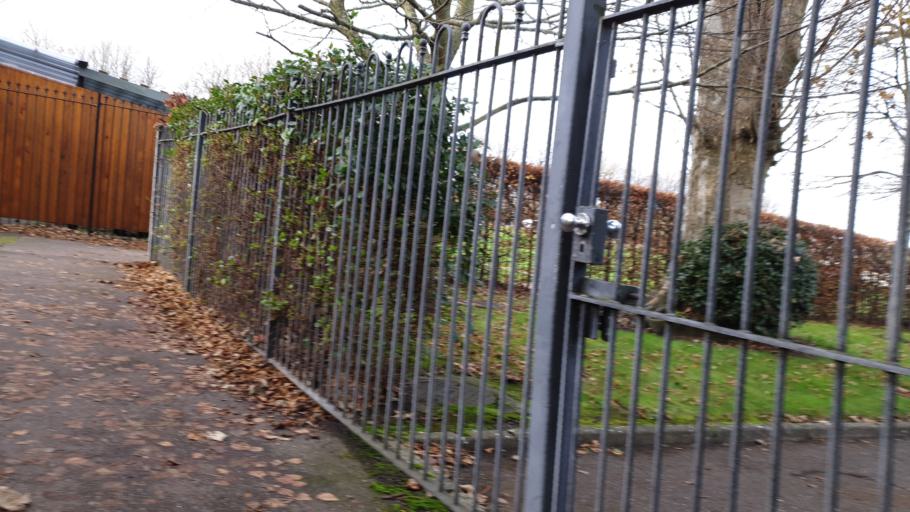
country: IE
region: Munster
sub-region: County Cork
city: Cork
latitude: 51.8954
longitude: -8.4121
